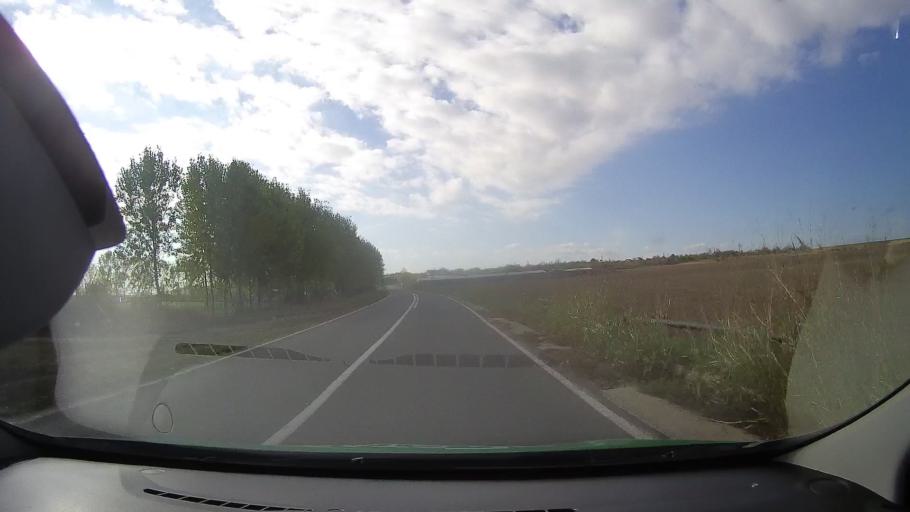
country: RO
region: Tulcea
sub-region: Comuna Sarichioi
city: Sarichioi
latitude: 44.9592
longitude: 28.8582
